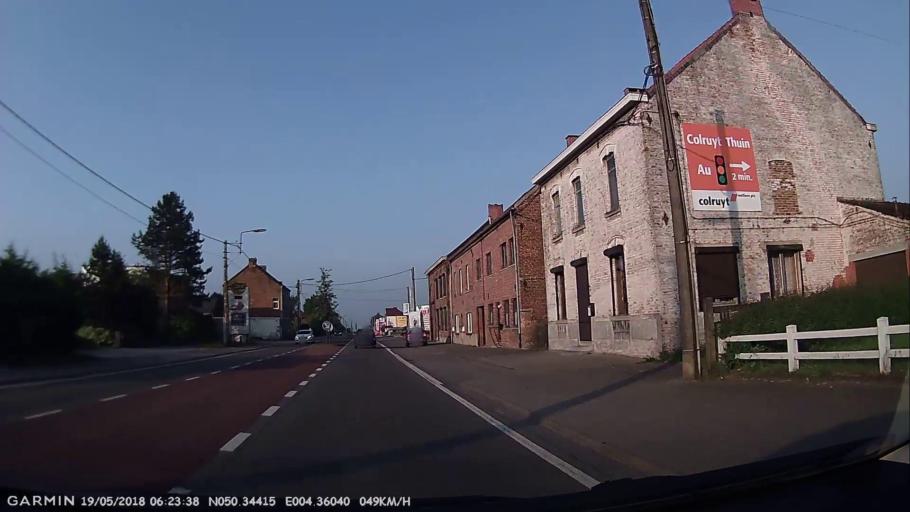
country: BE
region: Wallonia
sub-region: Province du Hainaut
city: Thuin
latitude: 50.3441
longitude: 4.3604
